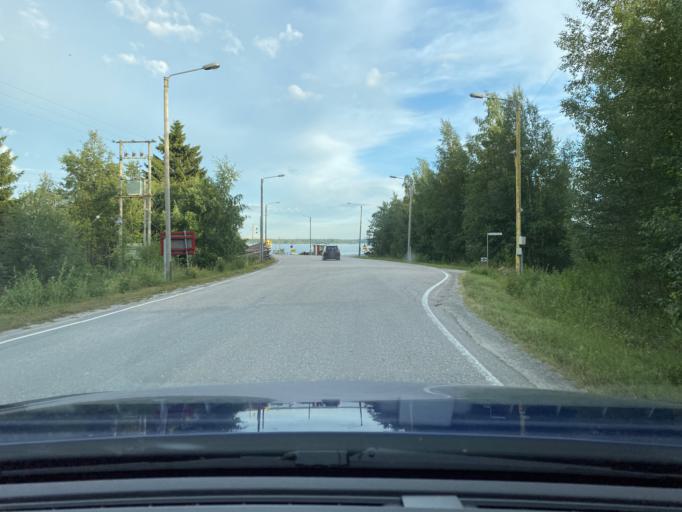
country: FI
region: Ostrobothnia
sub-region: Vaasa
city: Korsnaes
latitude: 62.9452
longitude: 21.1759
